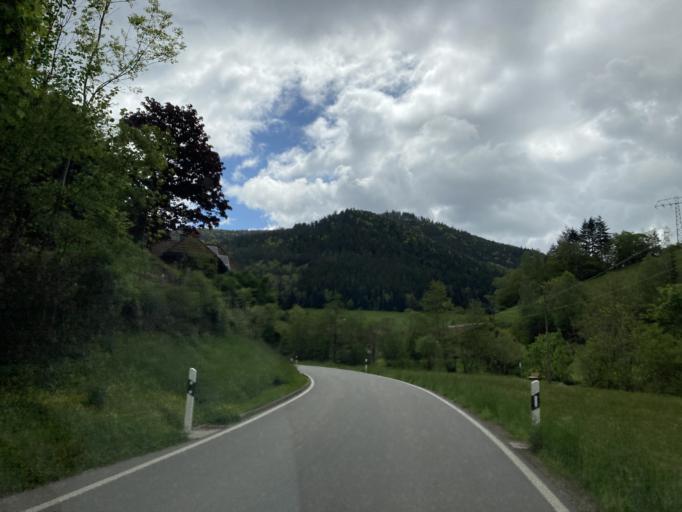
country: DE
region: Baden-Wuerttemberg
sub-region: Freiburg Region
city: Muhlenbach
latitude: 48.2061
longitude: 8.1572
